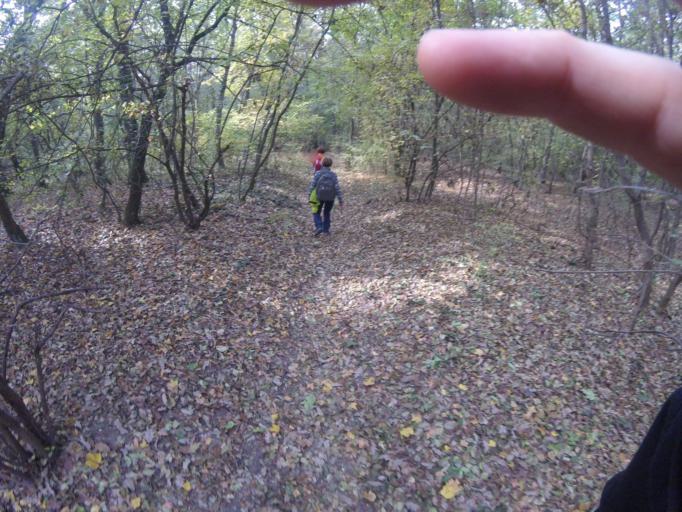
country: HU
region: Fejer
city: Bodajk
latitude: 47.3155
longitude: 18.2140
